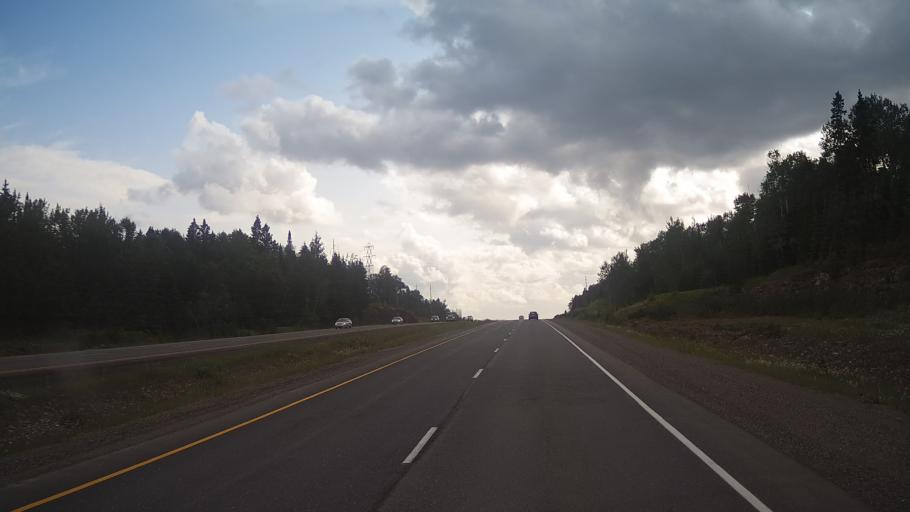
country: CA
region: Ontario
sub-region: Thunder Bay District
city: Thunder Bay
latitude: 48.4769
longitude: -89.1995
